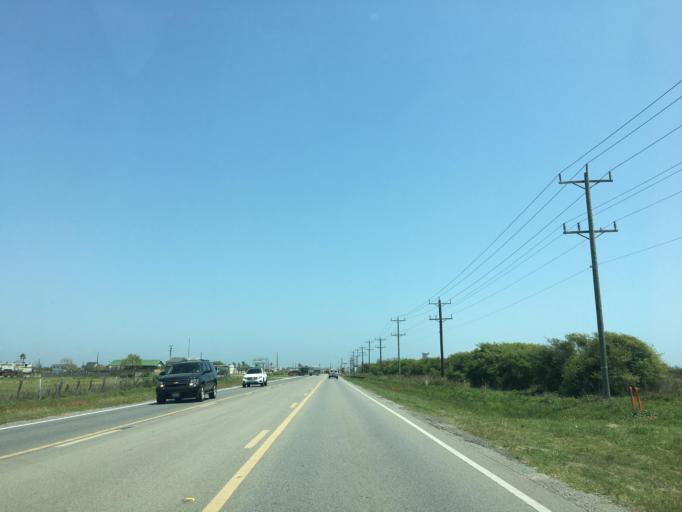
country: US
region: Texas
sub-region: Galveston County
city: Bolivar Peninsula
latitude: 29.4538
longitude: -94.6466
